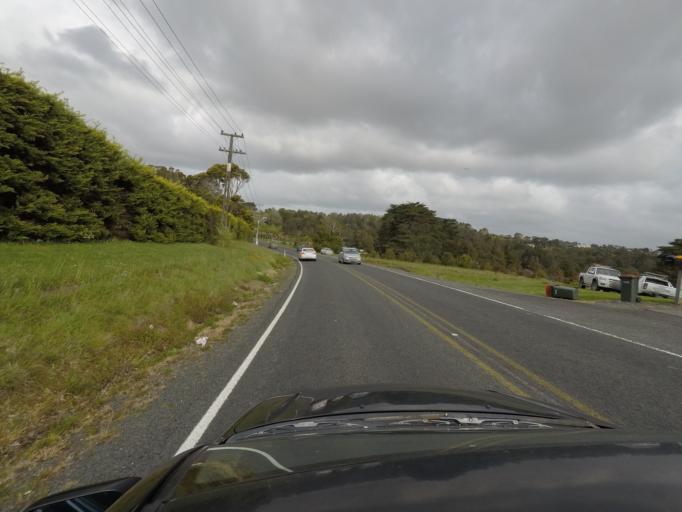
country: NZ
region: Auckland
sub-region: Auckland
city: Pakuranga
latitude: -36.9359
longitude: 174.9407
